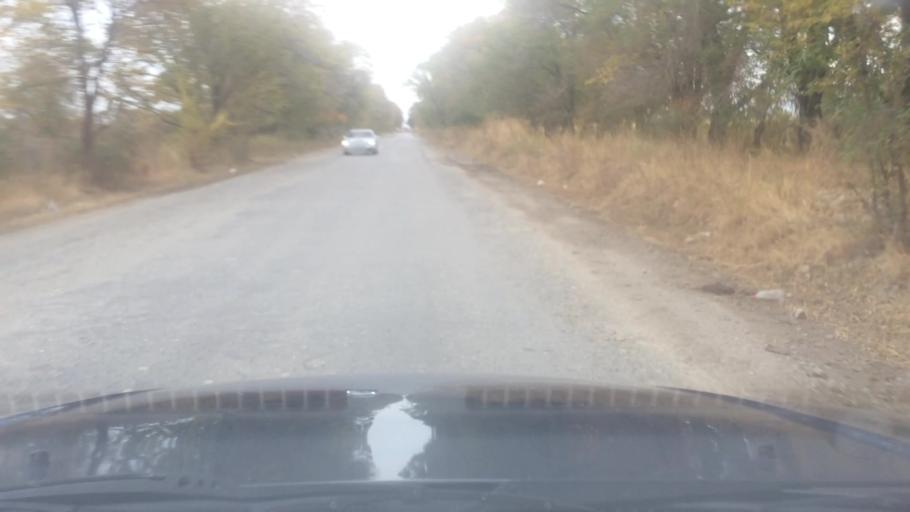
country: KG
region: Ysyk-Koel
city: Balykchy
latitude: 42.3048
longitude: 76.4744
